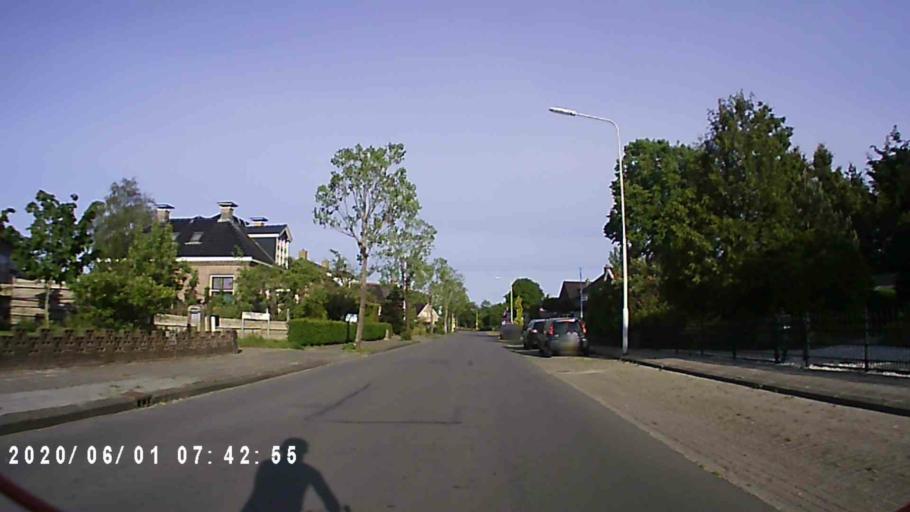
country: NL
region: Friesland
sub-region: Gemeente Dantumadiel
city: Damwald
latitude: 53.2905
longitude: 5.9758
